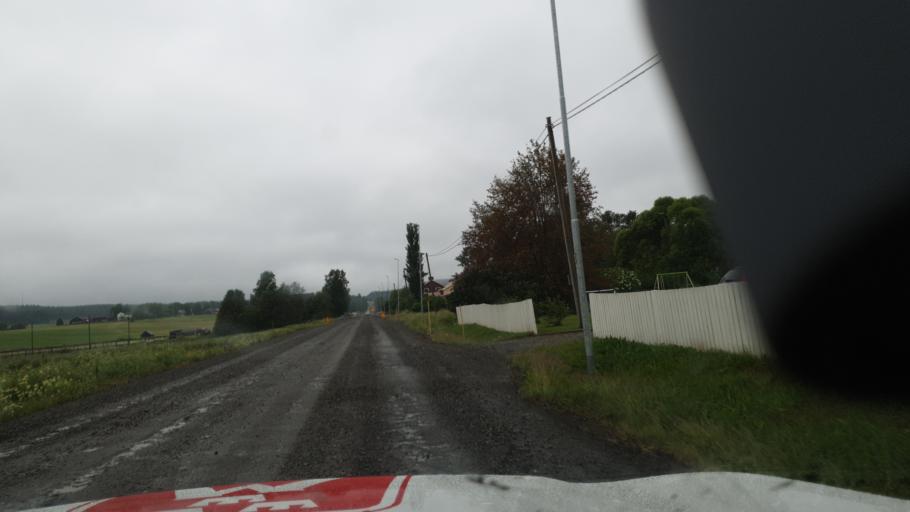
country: SE
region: Vaesterbotten
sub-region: Vannas Kommun
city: Vaennaes
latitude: 63.7581
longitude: 19.6333
